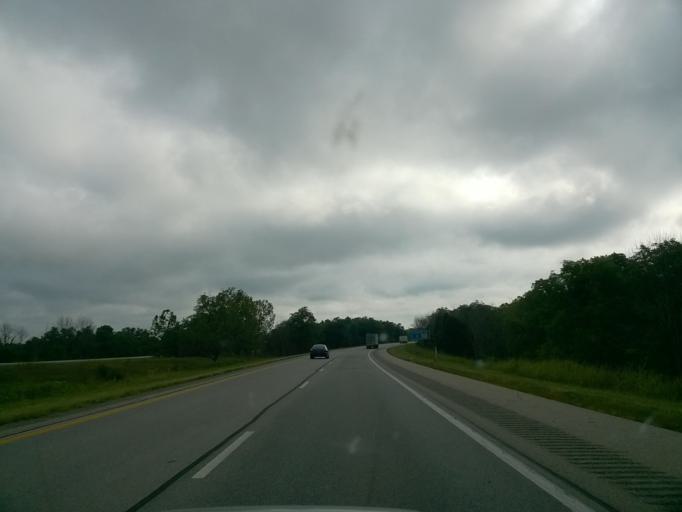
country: US
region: Indiana
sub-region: Floyd County
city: Georgetown
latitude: 38.2832
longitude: -85.9395
